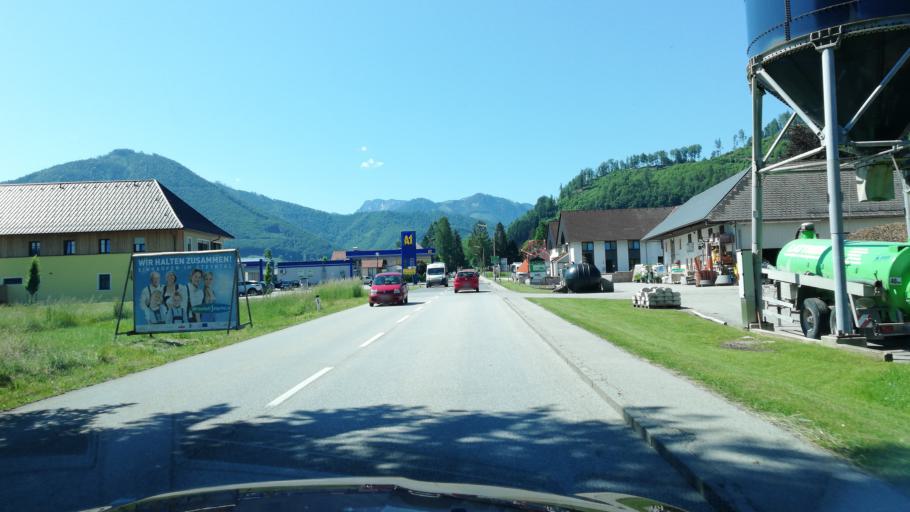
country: AT
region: Upper Austria
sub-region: Politischer Bezirk Kirchdorf an der Krems
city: Gruenburg
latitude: 47.8988
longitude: 14.2310
